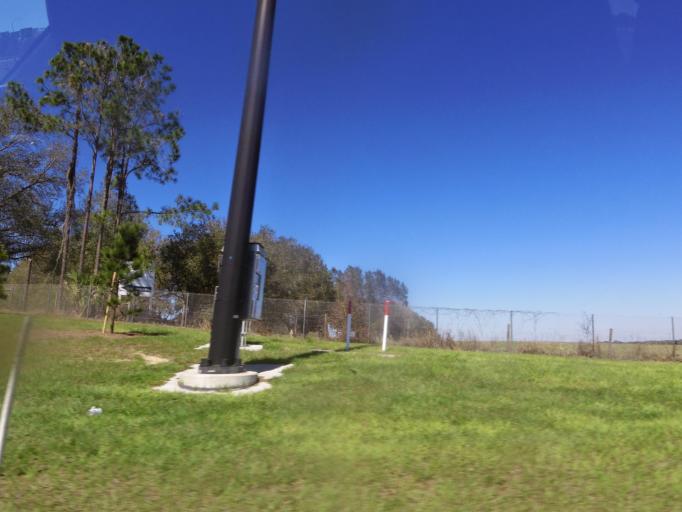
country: US
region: Florida
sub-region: Lake County
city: Mount Plymouth
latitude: 28.8043
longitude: -81.5882
